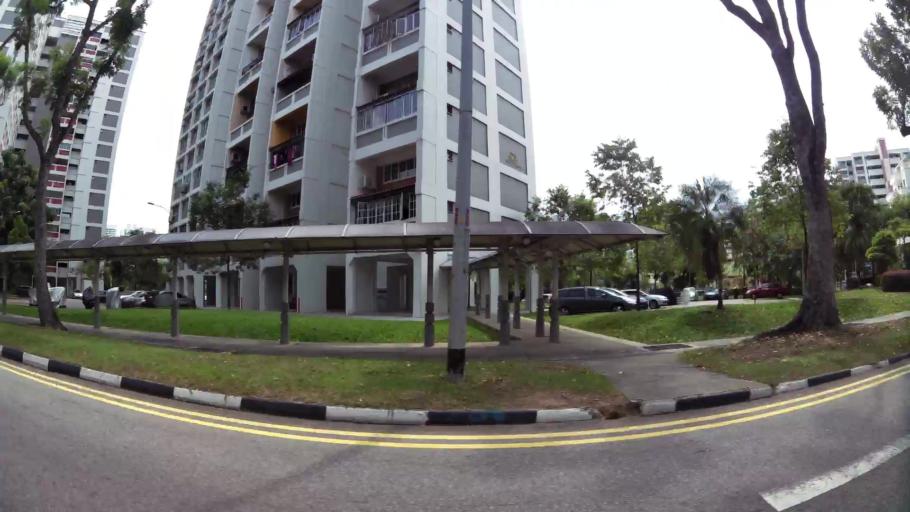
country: MY
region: Johor
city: Johor Bahru
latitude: 1.3501
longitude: 103.7425
